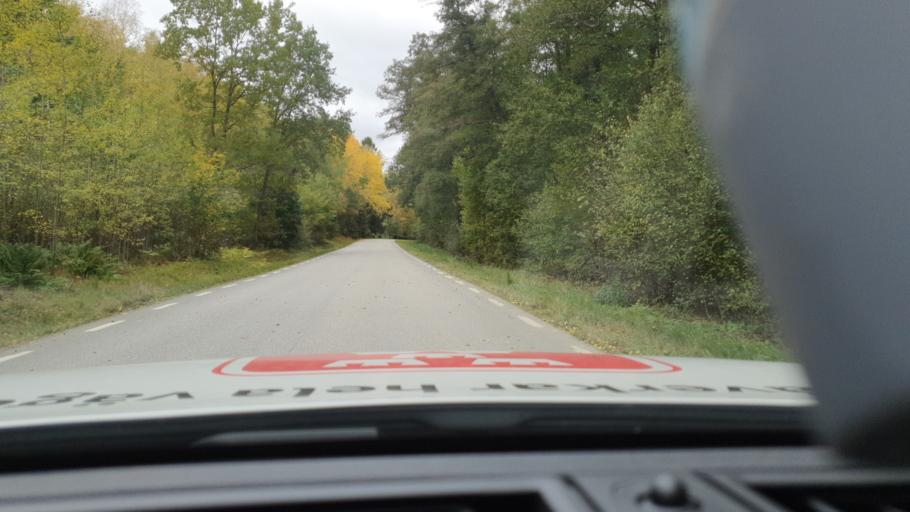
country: SE
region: Stockholm
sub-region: Upplands-Bro Kommun
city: Bro
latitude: 59.4999
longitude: 17.5669
